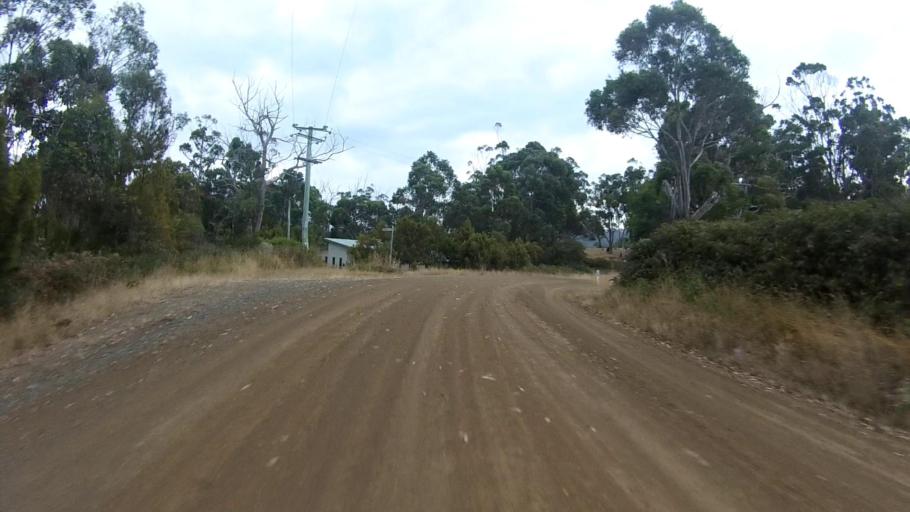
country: AU
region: Tasmania
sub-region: Huon Valley
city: Cygnet
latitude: -43.2349
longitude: 147.0990
